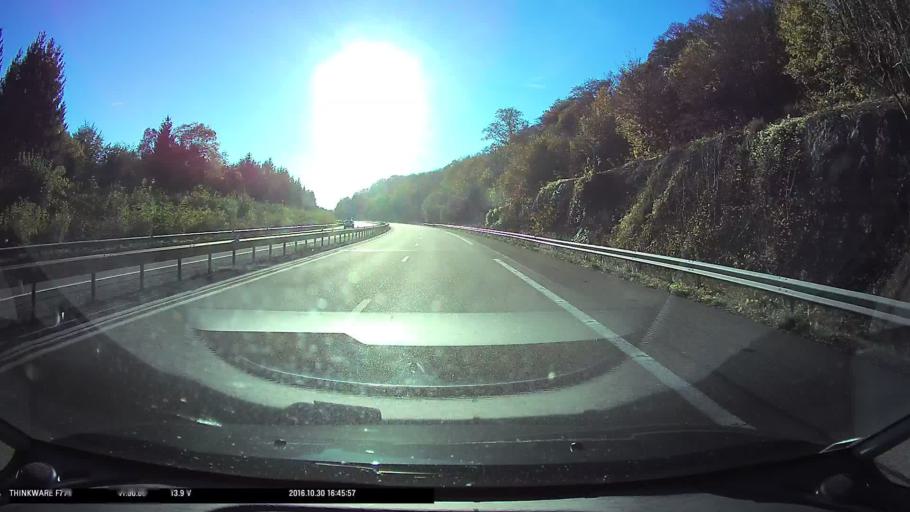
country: FR
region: Franche-Comte
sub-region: Departement du Doubs
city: Devecey
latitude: 47.3039
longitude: 6.0376
